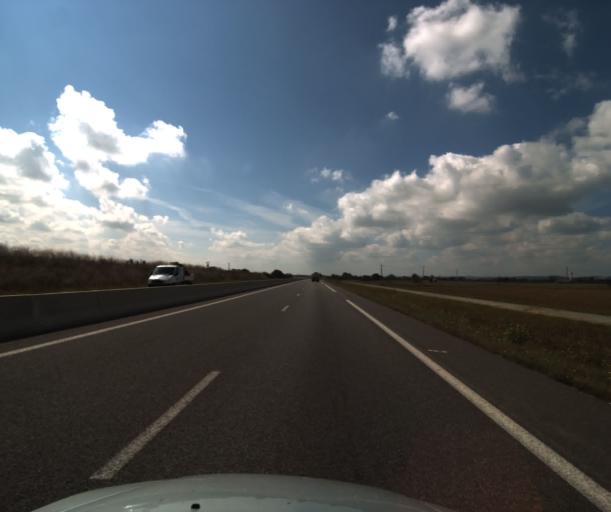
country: FR
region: Midi-Pyrenees
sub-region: Departement de la Haute-Garonne
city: Vernet
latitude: 43.4364
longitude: 1.4154
